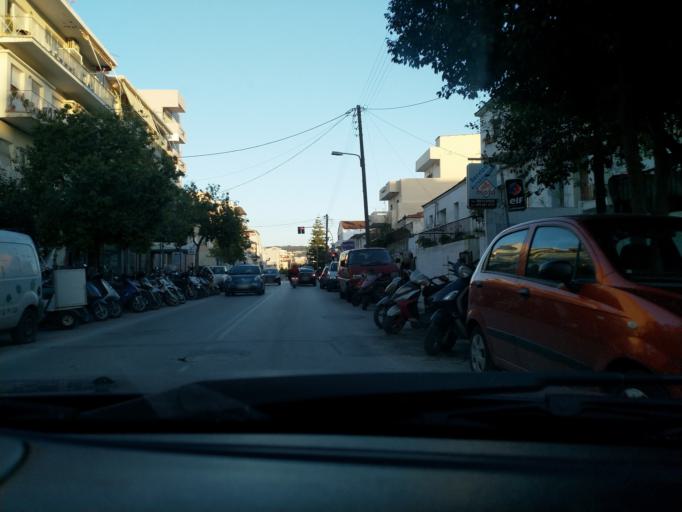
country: GR
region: Crete
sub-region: Nomos Chanias
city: Chania
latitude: 35.5104
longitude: 24.0193
